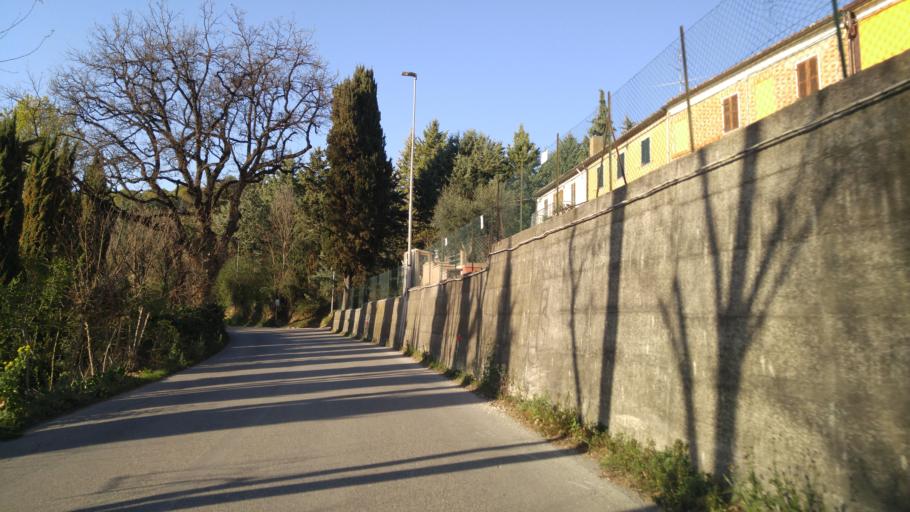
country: IT
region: The Marches
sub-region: Provincia di Pesaro e Urbino
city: Fenile
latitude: 43.8764
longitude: 12.9424
